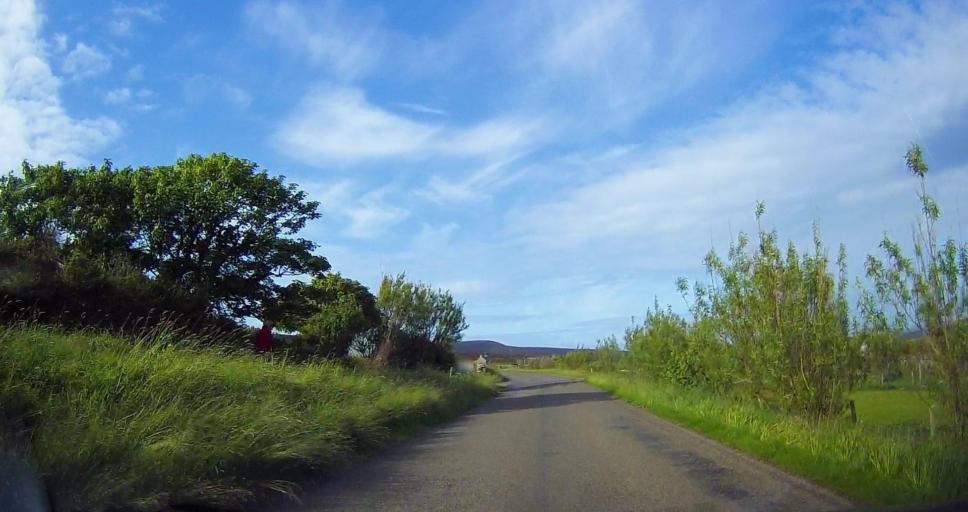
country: GB
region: Scotland
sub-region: Orkney Islands
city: Stromness
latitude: 58.7886
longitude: -3.2597
